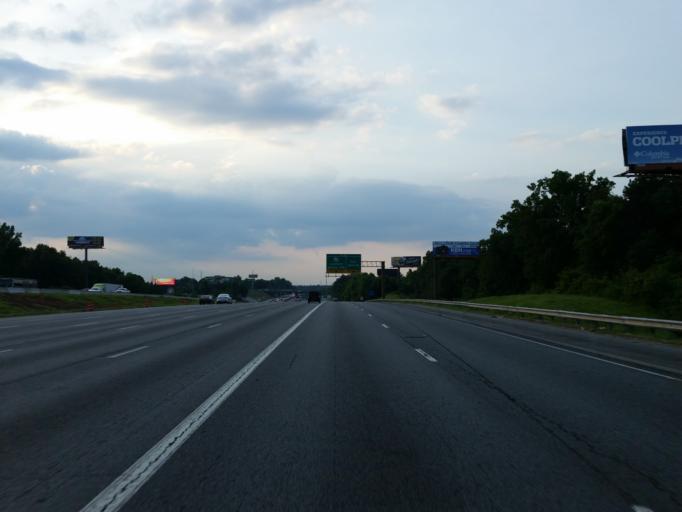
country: US
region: Georgia
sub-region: Cobb County
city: Smyrna
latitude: 33.9149
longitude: -84.4804
